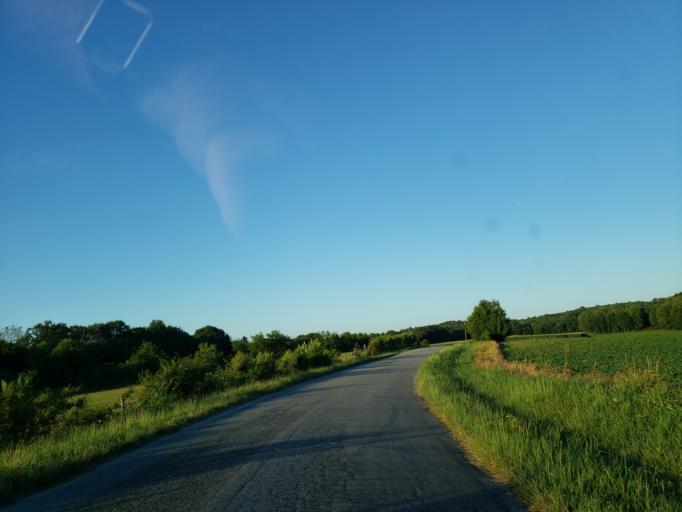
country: US
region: Georgia
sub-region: Bartow County
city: Euharlee
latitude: 34.0837
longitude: -84.9624
